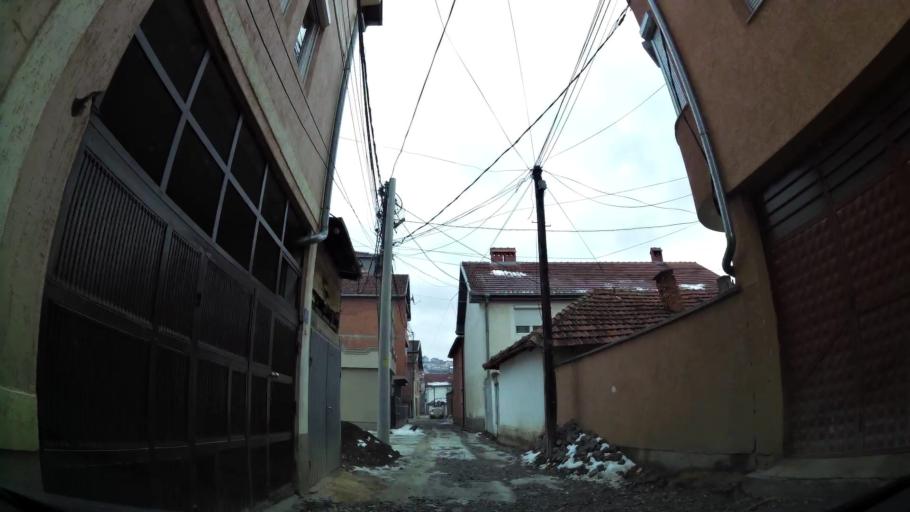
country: XK
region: Pristina
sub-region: Komuna e Prishtines
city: Pristina
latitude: 42.6739
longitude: 21.1697
